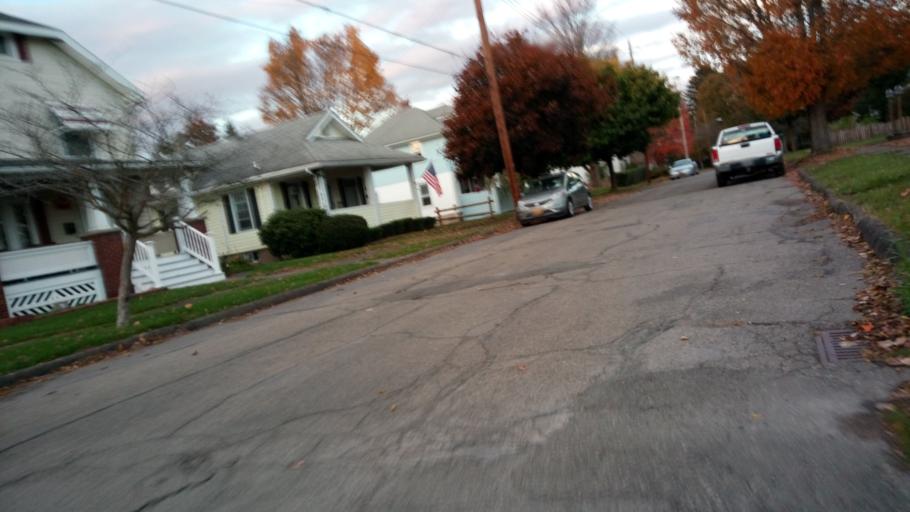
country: US
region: New York
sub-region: Chemung County
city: Elmira
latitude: 42.0747
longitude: -76.8156
